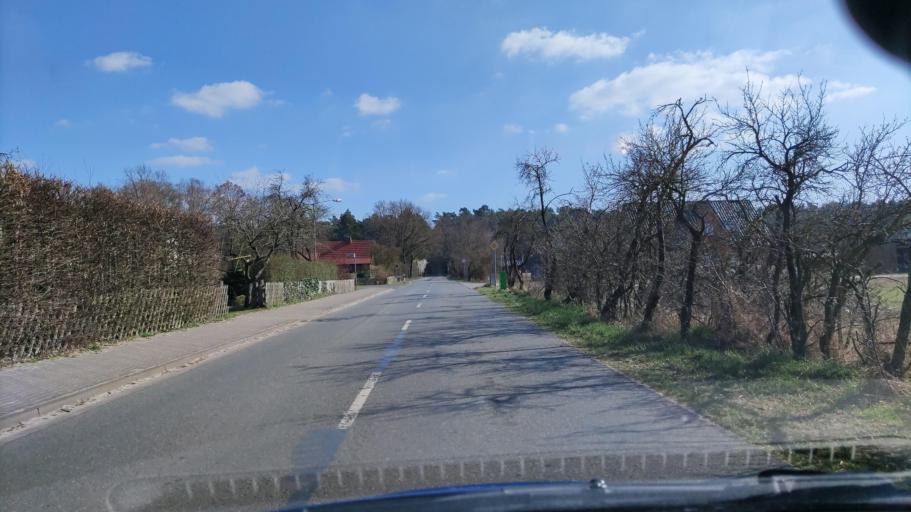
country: DE
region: Lower Saxony
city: Klein Gusborn
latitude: 53.1055
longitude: 11.2004
